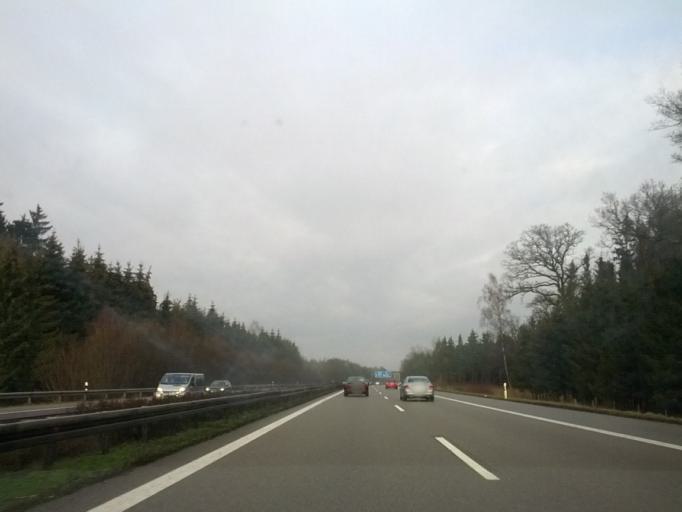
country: DE
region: Bavaria
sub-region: Swabia
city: Vohringen
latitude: 48.3066
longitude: 10.1010
